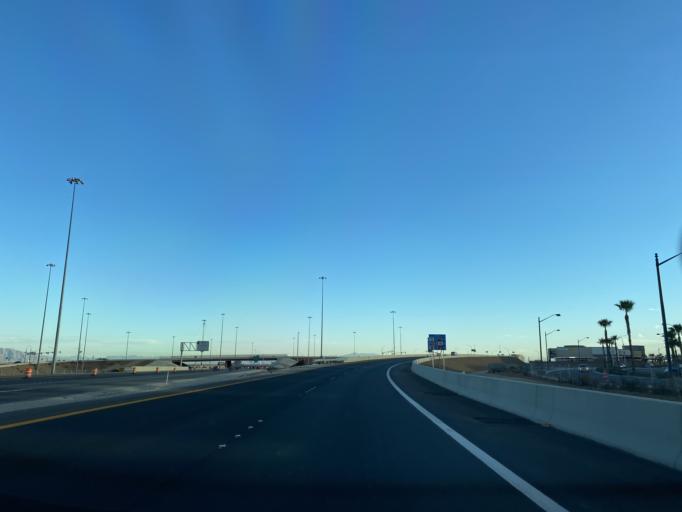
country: US
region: Nevada
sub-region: Clark County
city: Summerlin South
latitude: 36.3014
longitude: -115.2892
